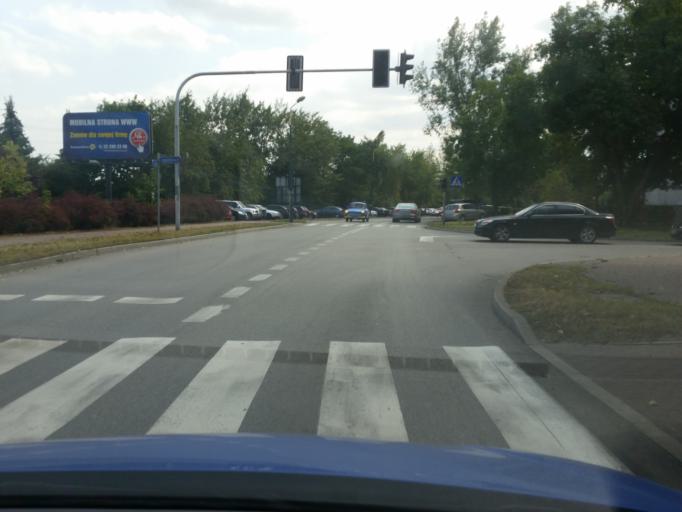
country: PL
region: Silesian Voivodeship
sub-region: Sosnowiec
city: Sosnowiec
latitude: 50.2675
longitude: 19.1372
